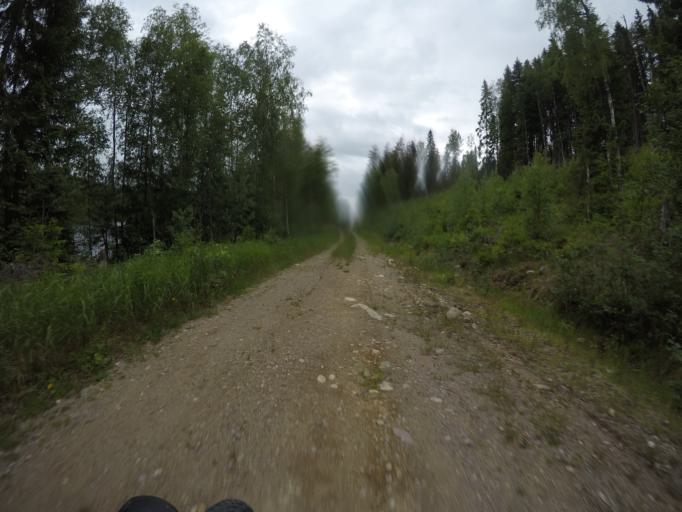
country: SE
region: Dalarna
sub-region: Ludvika Kommun
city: Abborrberget
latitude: 60.0490
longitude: 14.5898
